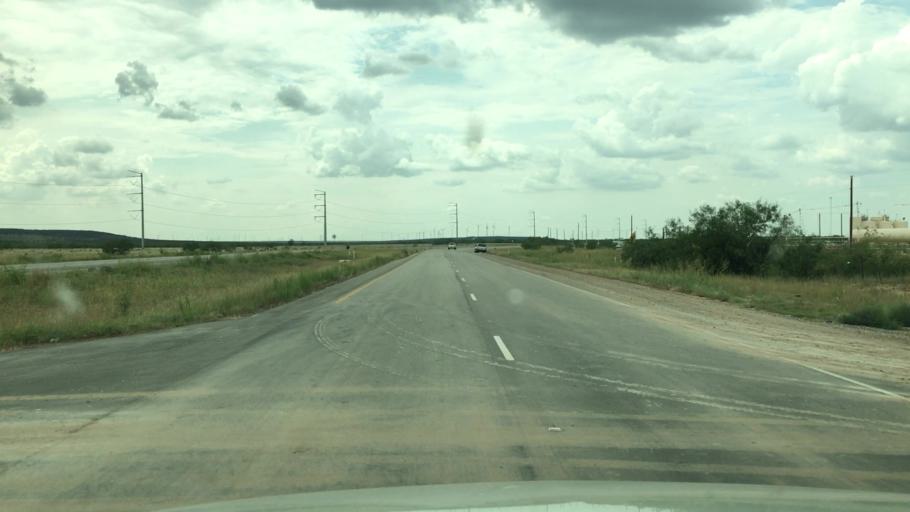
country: US
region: Texas
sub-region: Glasscock County
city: Garden City
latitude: 31.9678
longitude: -101.2359
